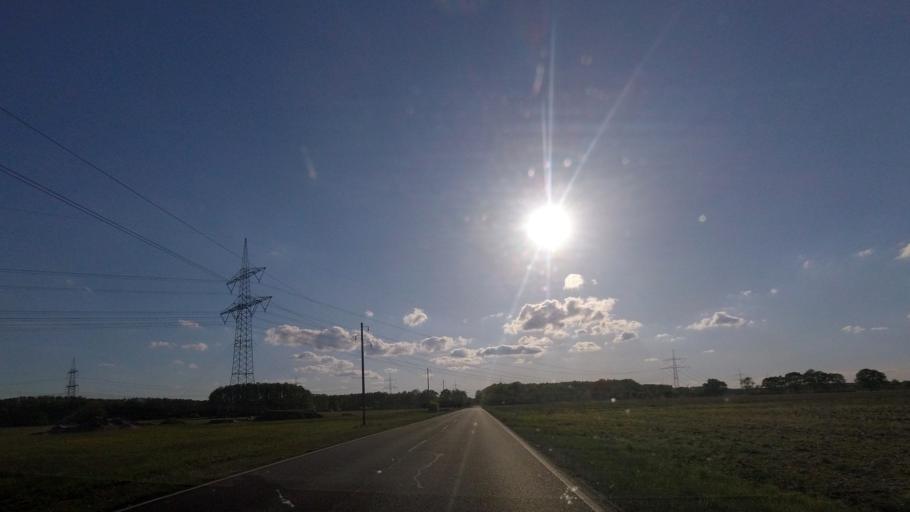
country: DE
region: Brandenburg
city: Luebben
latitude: 51.9048
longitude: 13.8449
